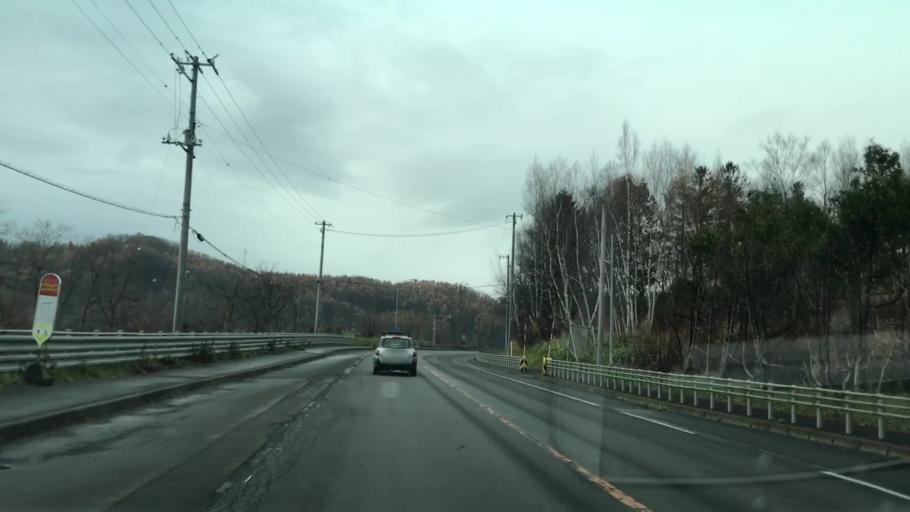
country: JP
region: Hokkaido
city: Yoichi
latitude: 43.2000
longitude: 140.8666
